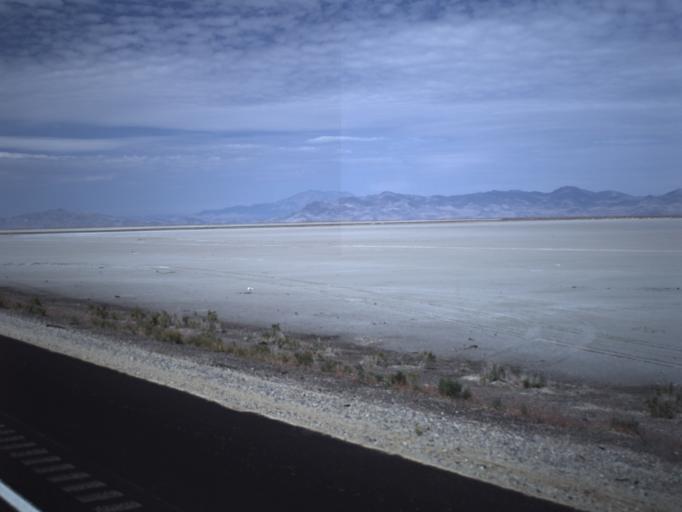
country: US
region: Utah
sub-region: Tooele County
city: Wendover
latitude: 40.7334
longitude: -113.5694
